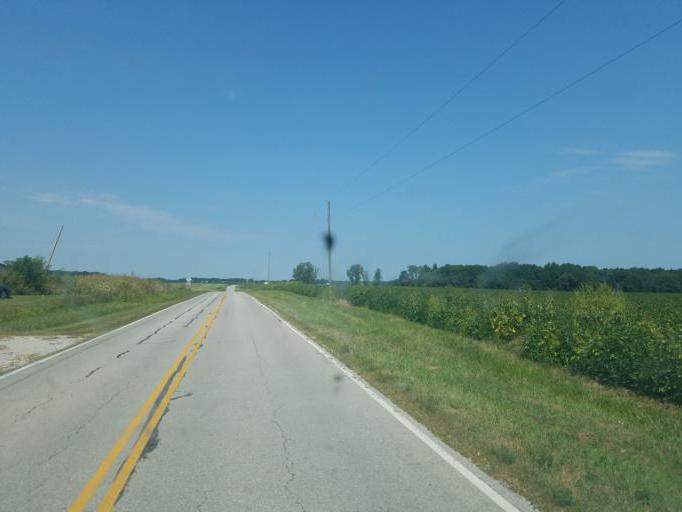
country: US
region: Ohio
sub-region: Marion County
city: Marion
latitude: 40.6736
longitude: -83.2320
